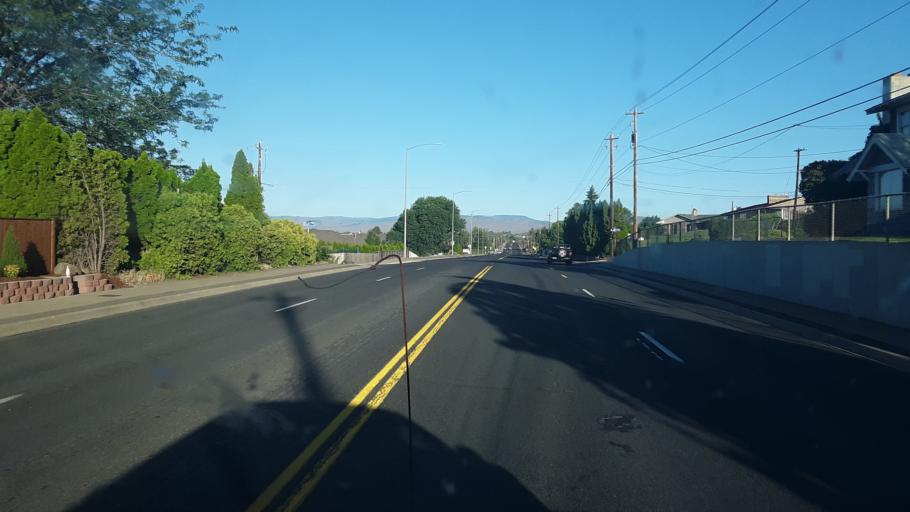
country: US
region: Washington
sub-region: Yakima County
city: West Valley
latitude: 46.6003
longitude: -120.6203
